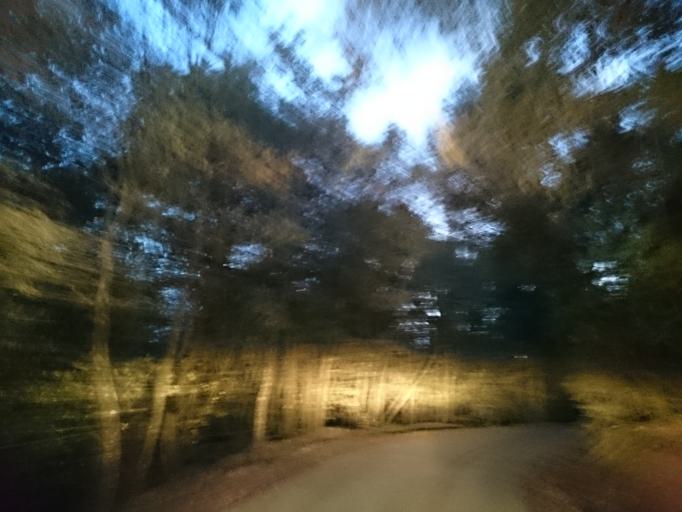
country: ES
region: Catalonia
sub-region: Provincia de Barcelona
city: Tavertet
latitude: 41.9995
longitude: 2.4543
